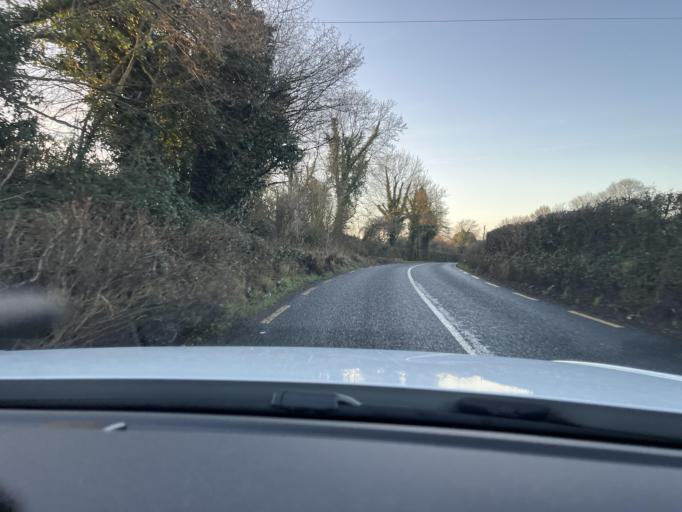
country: IE
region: Ulster
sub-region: An Cabhan
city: Ballyconnell
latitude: 54.0919
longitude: -7.6314
